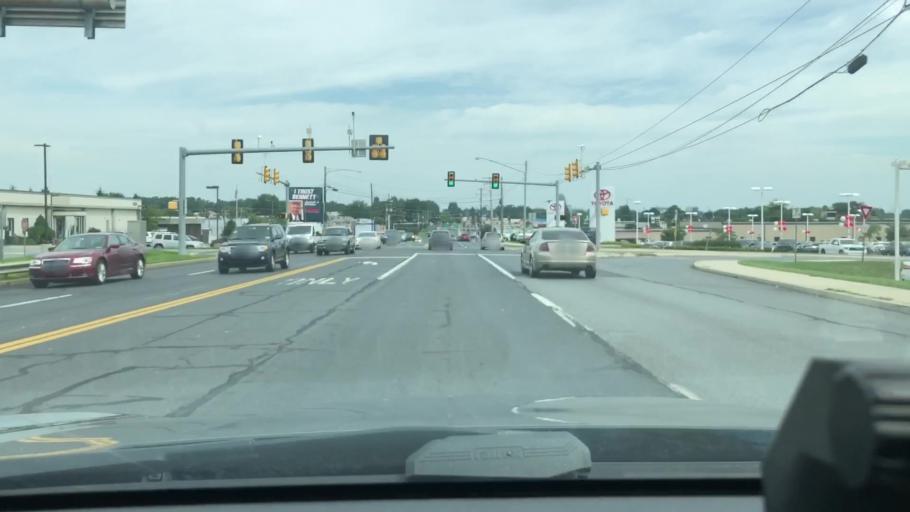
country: US
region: Pennsylvania
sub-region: Lehigh County
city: Allentown
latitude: 40.5733
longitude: -75.4807
